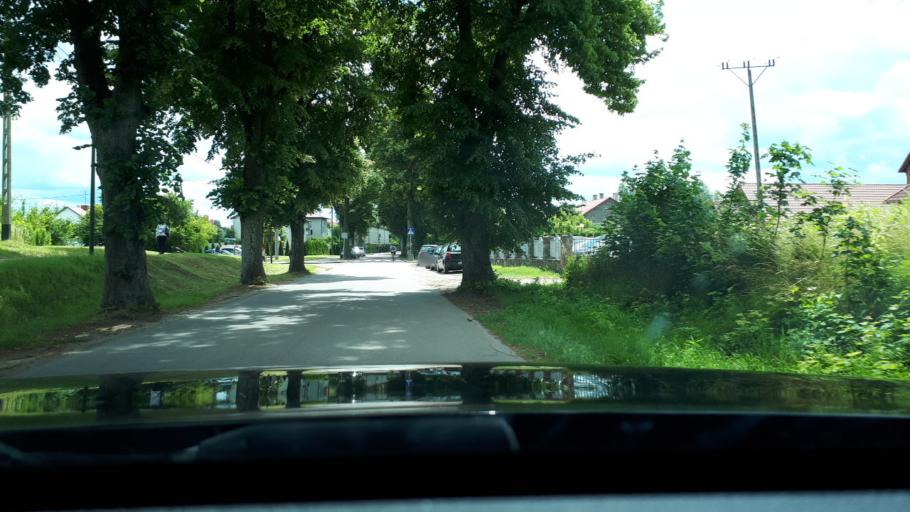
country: PL
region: Warmian-Masurian Voivodeship
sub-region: Powiat olsztynski
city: Olsztynek
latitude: 53.5888
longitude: 20.2790
